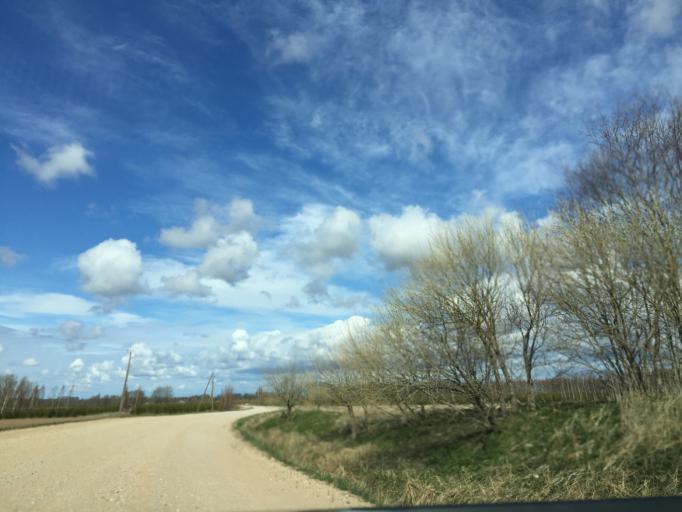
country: LV
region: Limbazu Rajons
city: Limbazi
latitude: 57.5883
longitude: 24.5992
